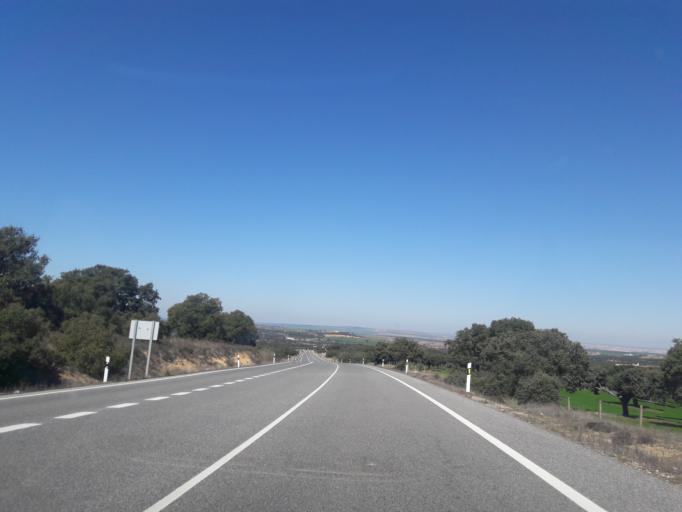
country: ES
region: Castille and Leon
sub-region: Provincia de Salamanca
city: Martinamor
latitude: 40.8164
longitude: -5.6296
